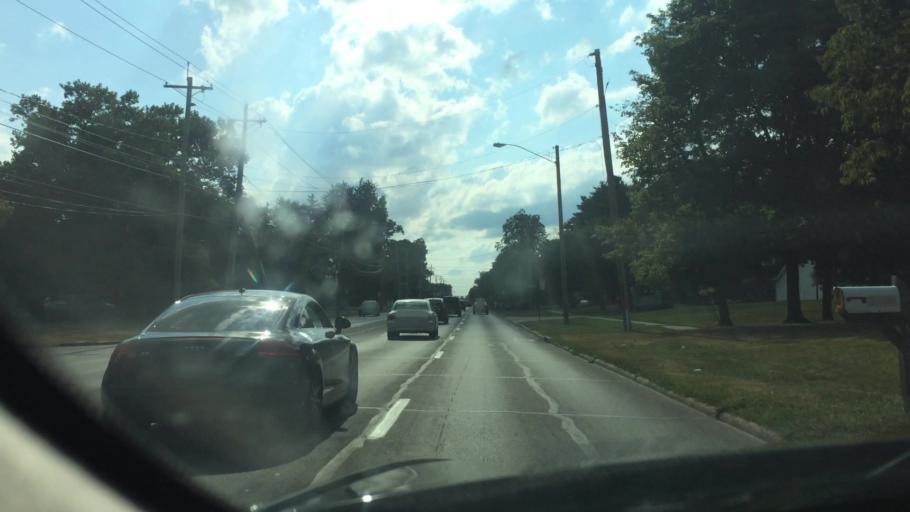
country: US
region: Ohio
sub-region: Lucas County
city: Maumee
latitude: 41.5946
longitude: -83.6569
